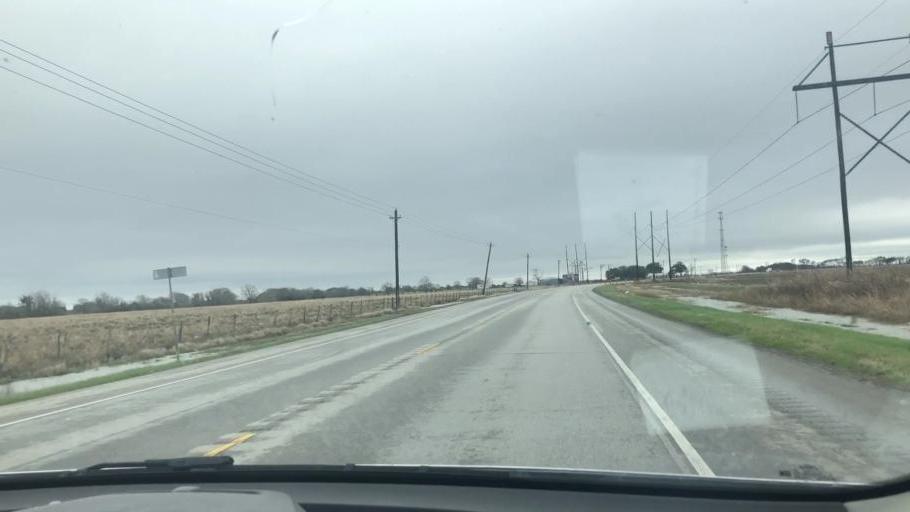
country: US
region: Texas
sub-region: Wharton County
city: Boling
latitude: 29.1456
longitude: -95.9902
